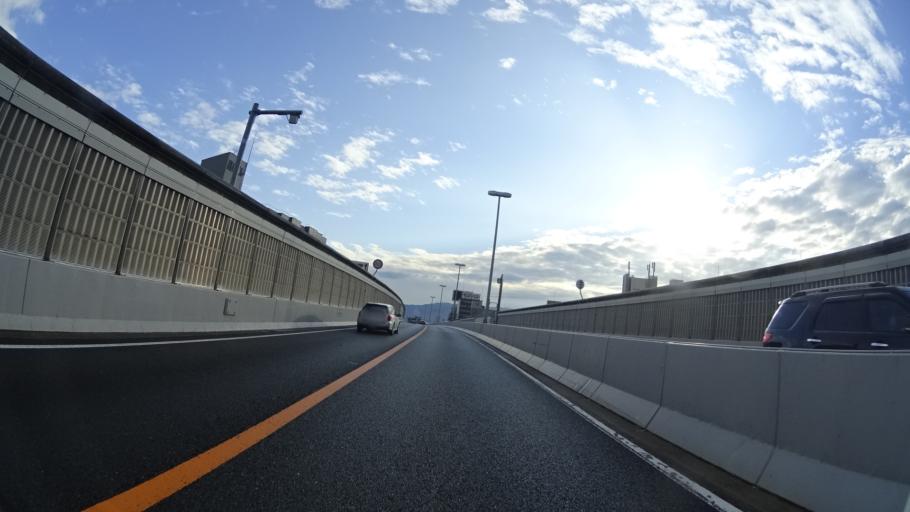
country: JP
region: Osaka
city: Moriguchi
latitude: 34.6783
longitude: 135.5712
